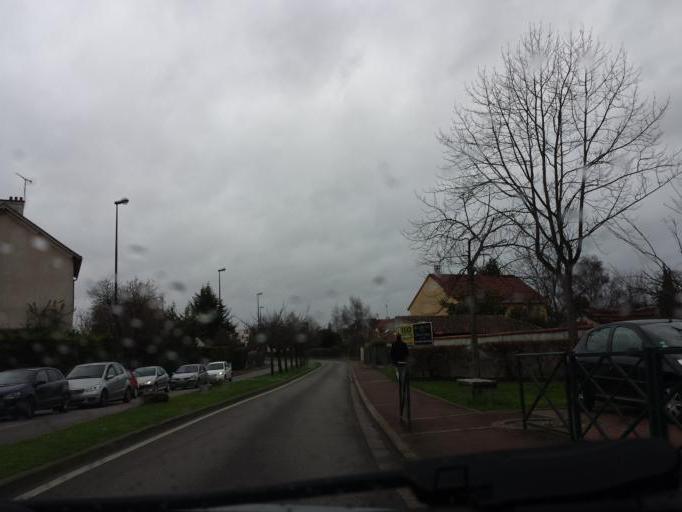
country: FR
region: Ile-de-France
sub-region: Departement du Val-d'Oise
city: Franconville
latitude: 48.9890
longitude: 2.2297
